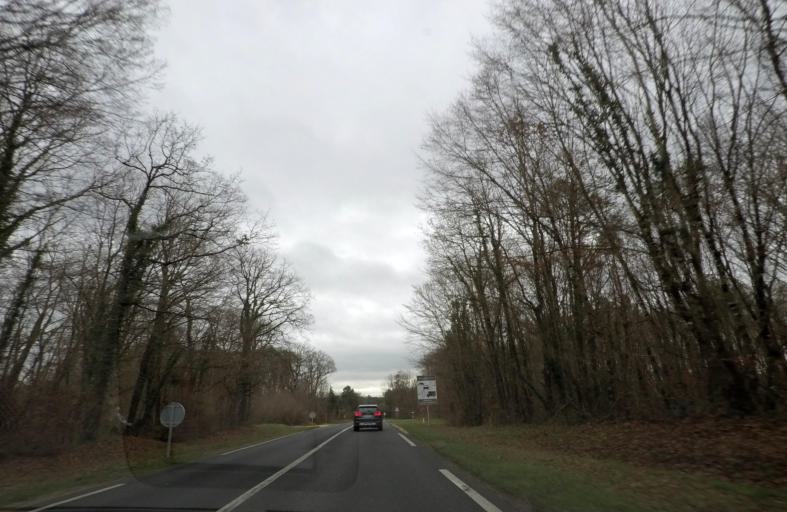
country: FR
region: Centre
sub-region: Departement du Loir-et-Cher
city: Cellettes
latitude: 47.5355
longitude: 1.4139
